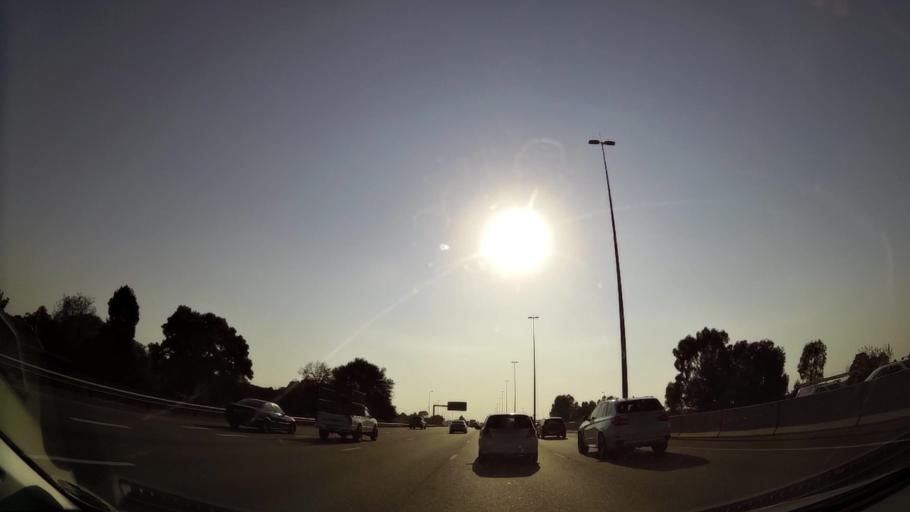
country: ZA
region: Gauteng
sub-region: City of Tshwane Metropolitan Municipality
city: Centurion
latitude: -25.8354
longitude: 28.2374
